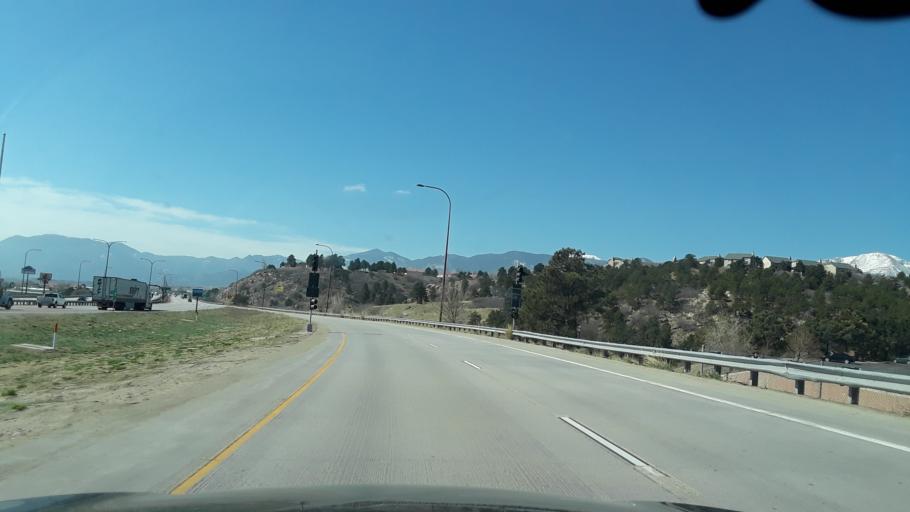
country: US
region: Colorado
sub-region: El Paso County
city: Colorado Springs
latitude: 38.9099
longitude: -104.8251
